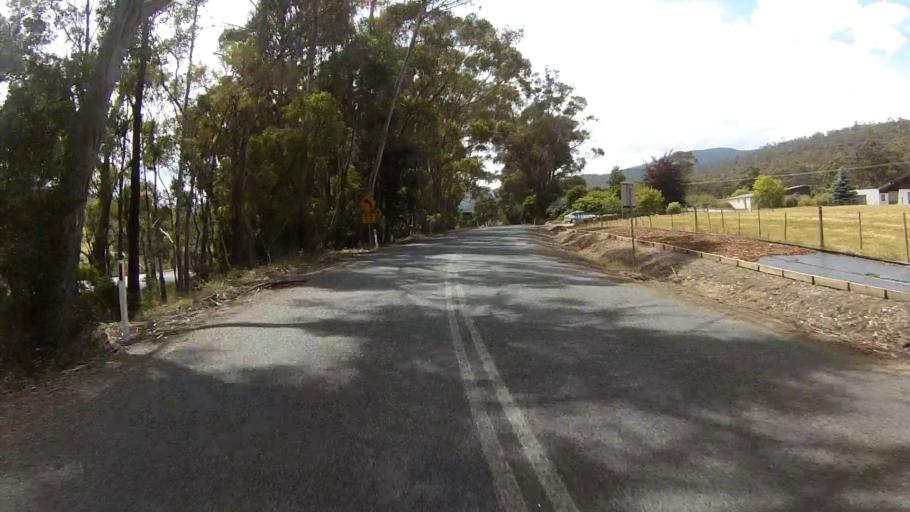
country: AU
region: Tasmania
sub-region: Huon Valley
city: Cygnet
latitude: -43.1864
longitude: 147.1049
